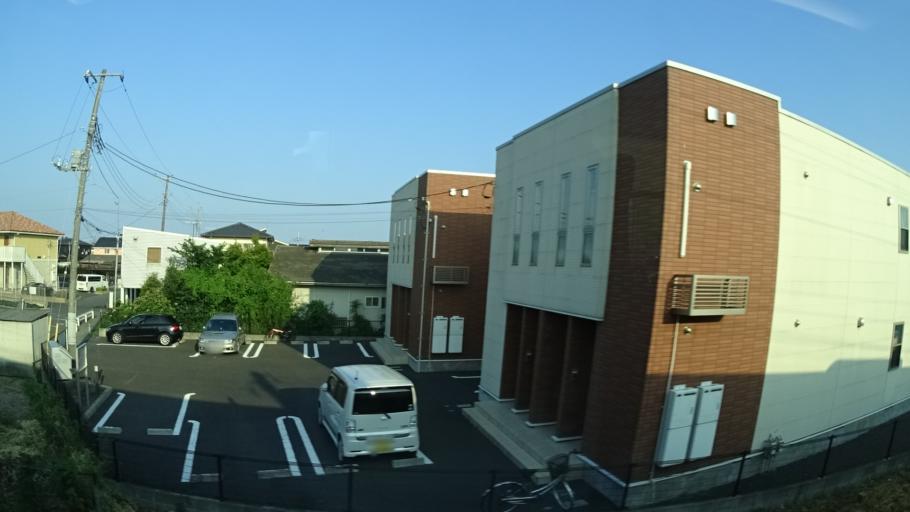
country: JP
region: Ibaraki
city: Funaishikawa
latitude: 36.4713
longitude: 140.5734
